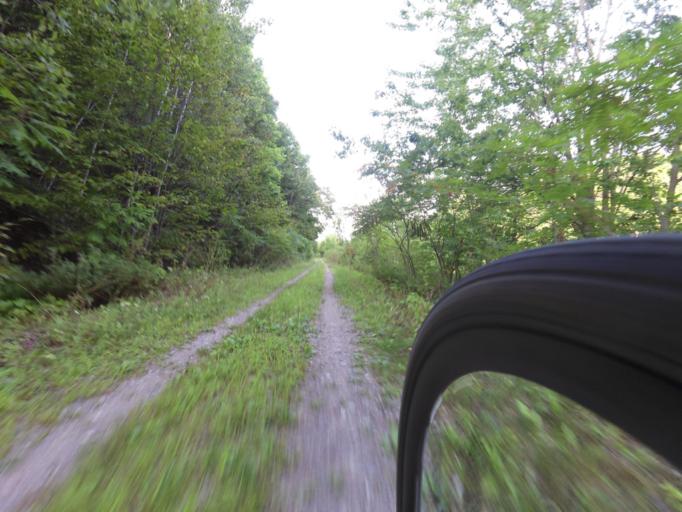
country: CA
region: Ontario
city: Kingston
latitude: 44.5135
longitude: -76.4204
